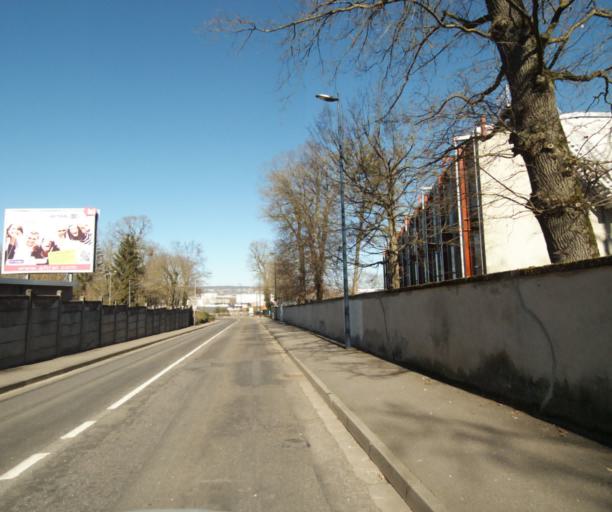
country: FR
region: Lorraine
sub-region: Departement de Meurthe-et-Moselle
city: Jarville-la-Malgrange
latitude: 48.6660
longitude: 6.2082
